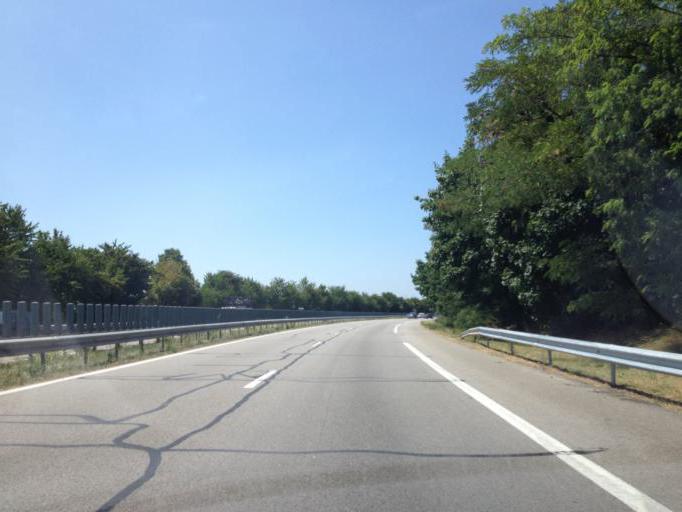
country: FR
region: Rhone-Alpes
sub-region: Departement de la Drome
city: Saint-Marcel-les-Valence
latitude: 44.9654
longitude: 4.9599
